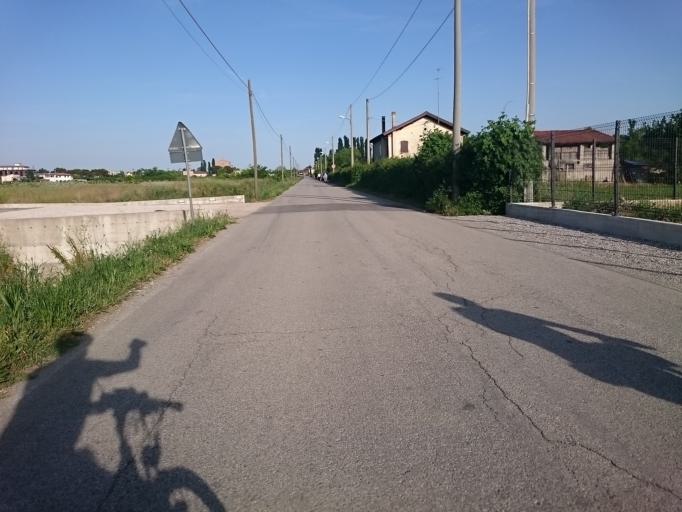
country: IT
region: Veneto
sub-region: Provincia di Padova
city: Mandriola-Sant'Agostino
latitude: 45.3653
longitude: 11.8359
